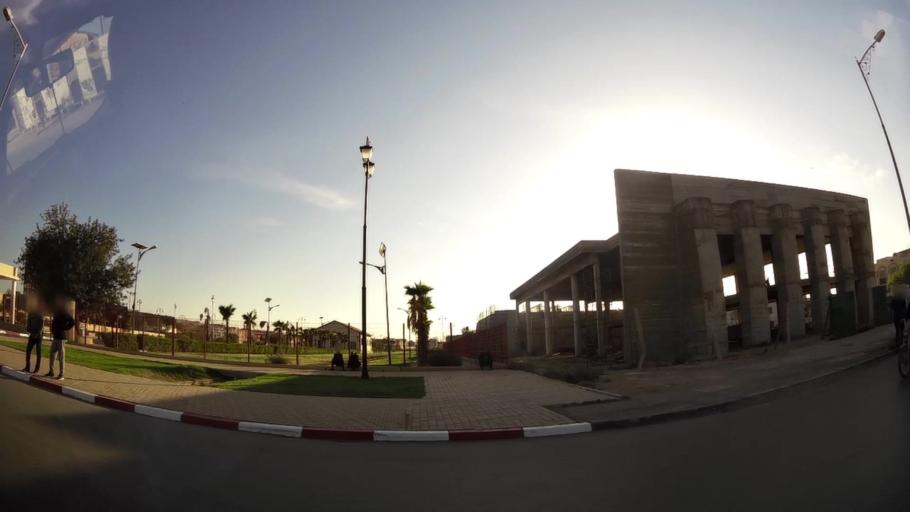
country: MA
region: Oriental
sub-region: Oujda-Angad
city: Oujda
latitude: 34.6985
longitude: -1.9103
